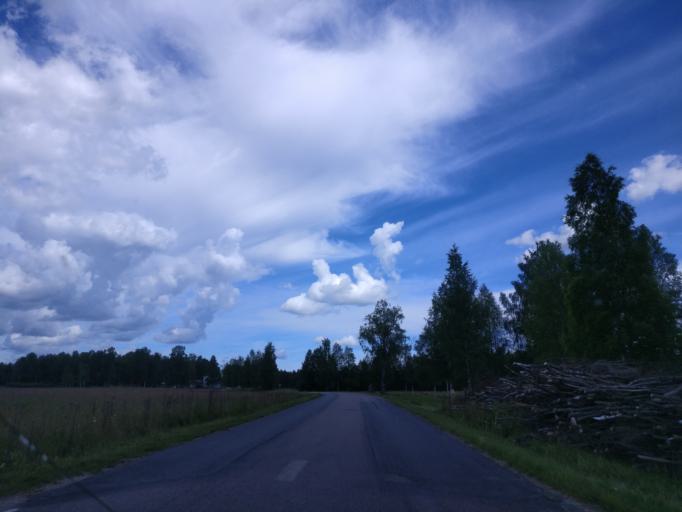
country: SE
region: Vaermland
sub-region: Hagfors Kommun
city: Ekshaerad
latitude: 60.1283
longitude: 13.4572
